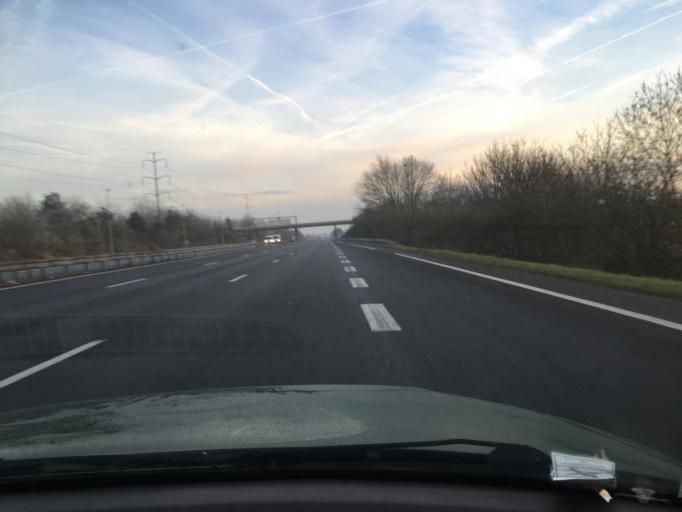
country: FR
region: Centre
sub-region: Departement du Loiret
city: Baule
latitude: 47.8350
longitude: 1.6674
